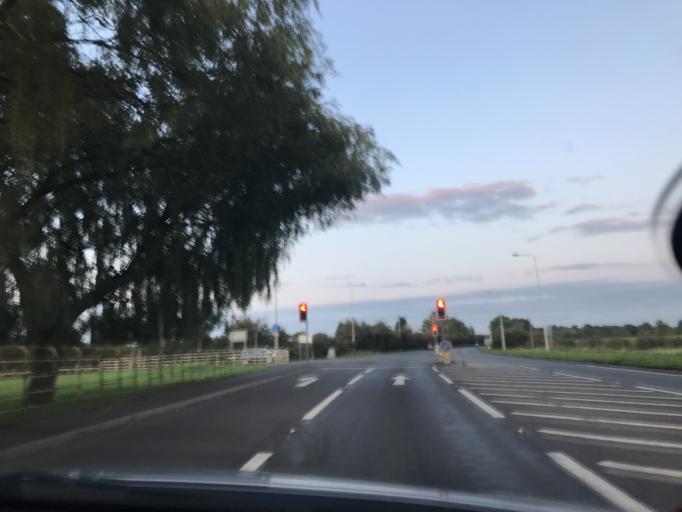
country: GB
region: England
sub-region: Cheshire West and Chester
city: Guilden Sutton
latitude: 53.2002
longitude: -2.7996
